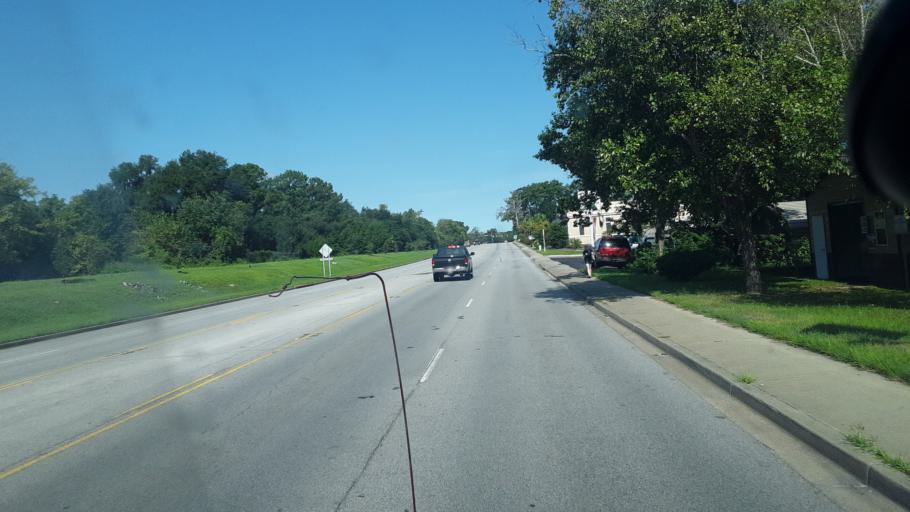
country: US
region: South Carolina
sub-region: Beaufort County
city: Burton
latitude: 32.4404
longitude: -80.7164
